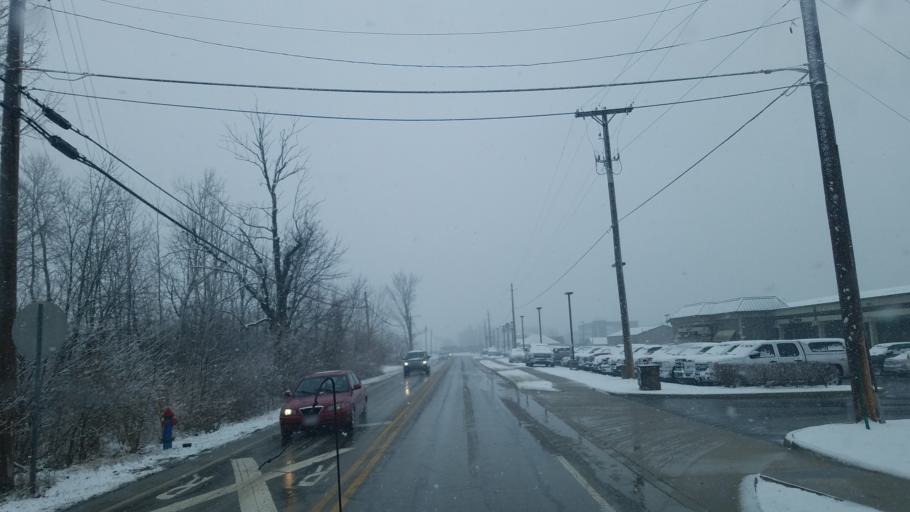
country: US
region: Ohio
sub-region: Union County
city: Marysville
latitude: 40.2354
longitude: -83.3521
